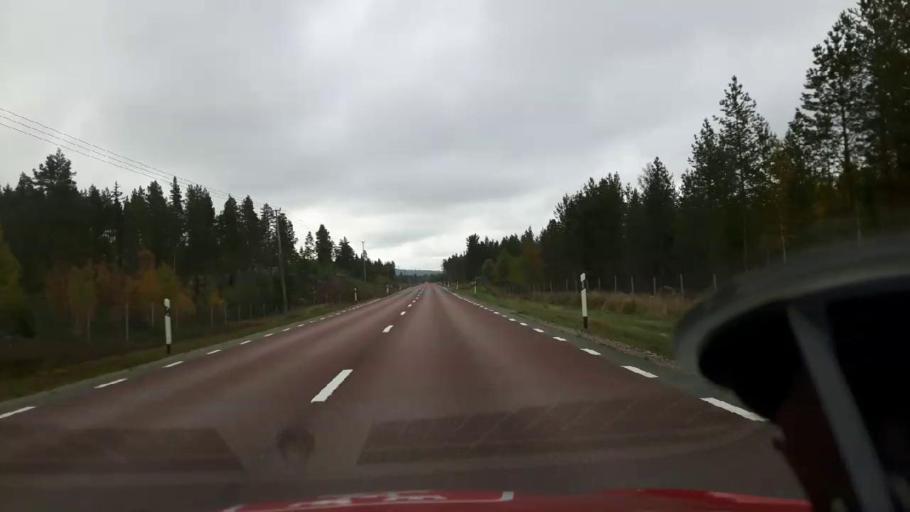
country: SE
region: Jaemtland
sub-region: Harjedalens Kommun
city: Sveg
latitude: 62.2368
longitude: 14.8346
